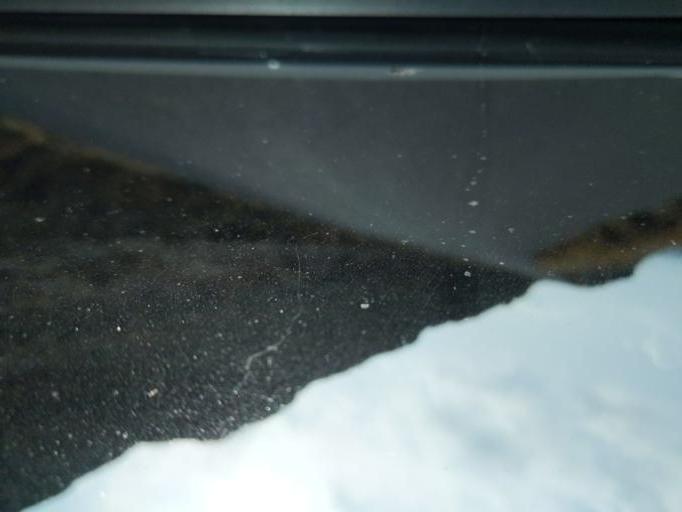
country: GR
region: Crete
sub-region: Nomos Lasithiou
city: Palekastro
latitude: 35.0897
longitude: 26.2623
